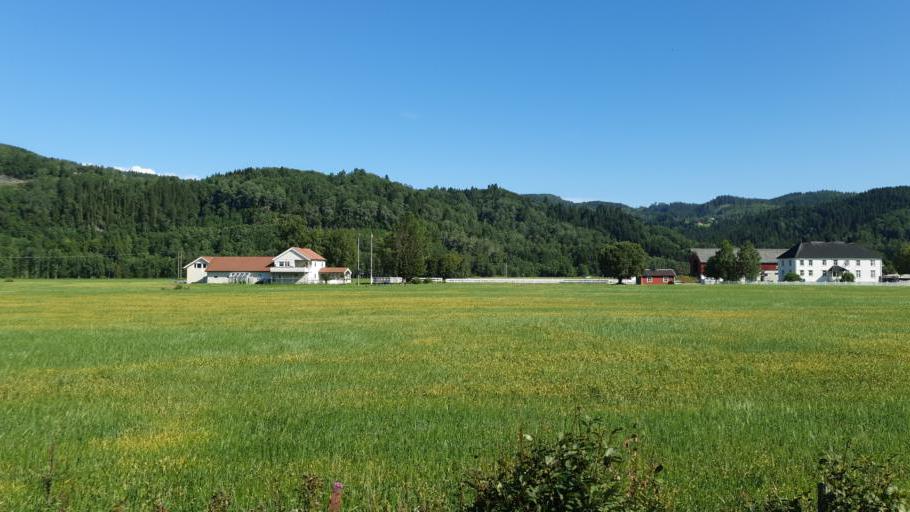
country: NO
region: Sor-Trondelag
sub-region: Orkdal
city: Orkanger
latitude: 63.2047
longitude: 9.7840
